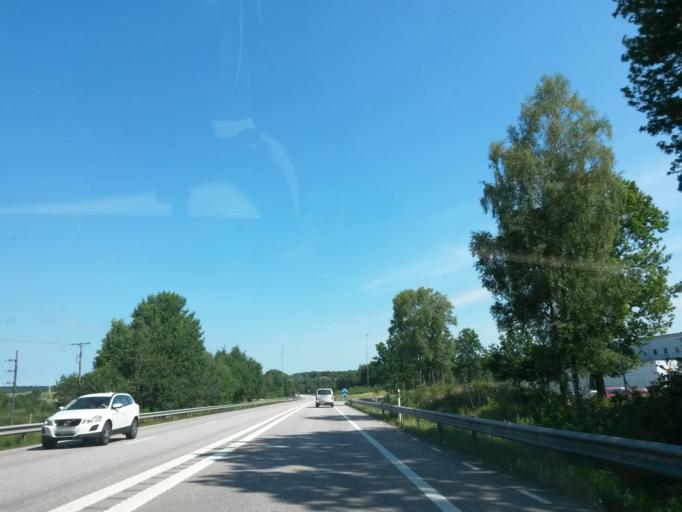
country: SE
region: Vaestra Goetaland
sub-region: Vargarda Kommun
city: Vargarda
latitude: 58.0214
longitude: 12.7812
